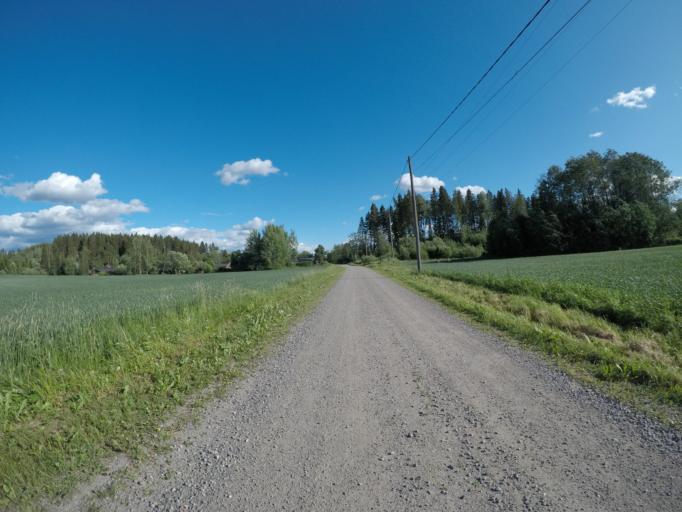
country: FI
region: Haeme
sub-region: Haemeenlinna
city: Haemeenlinna
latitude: 61.0217
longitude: 24.4991
